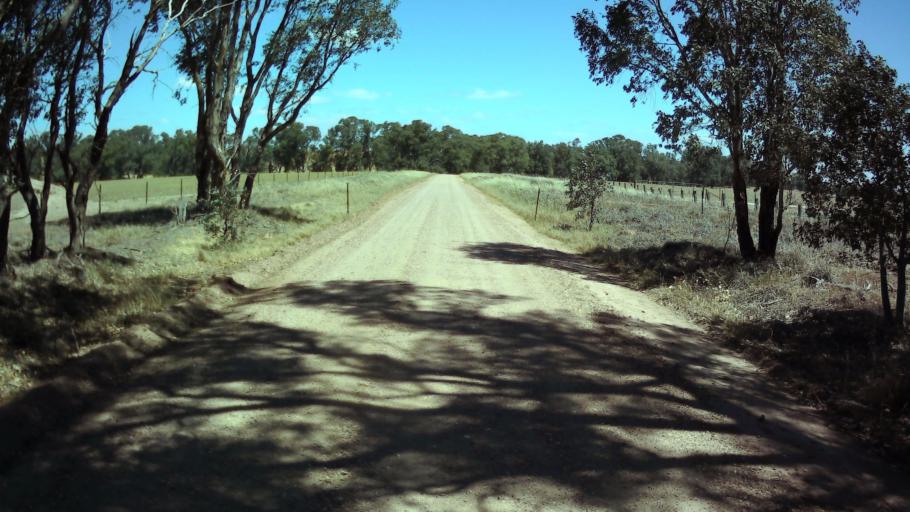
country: AU
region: New South Wales
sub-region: Weddin
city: Grenfell
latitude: -33.9301
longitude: 148.3346
